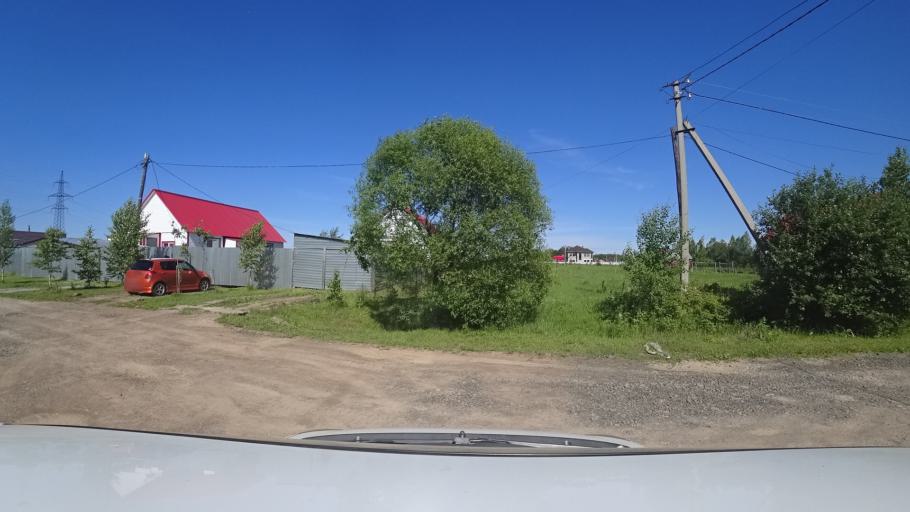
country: RU
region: Khabarovsk Krai
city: Topolevo
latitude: 48.5534
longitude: 135.1690
